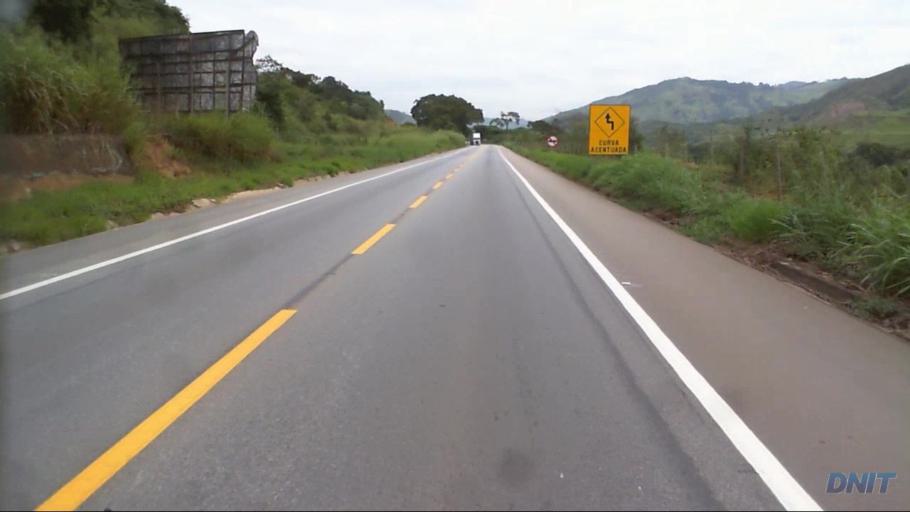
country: BR
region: Minas Gerais
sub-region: Timoteo
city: Timoteo
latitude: -19.5795
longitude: -42.7243
